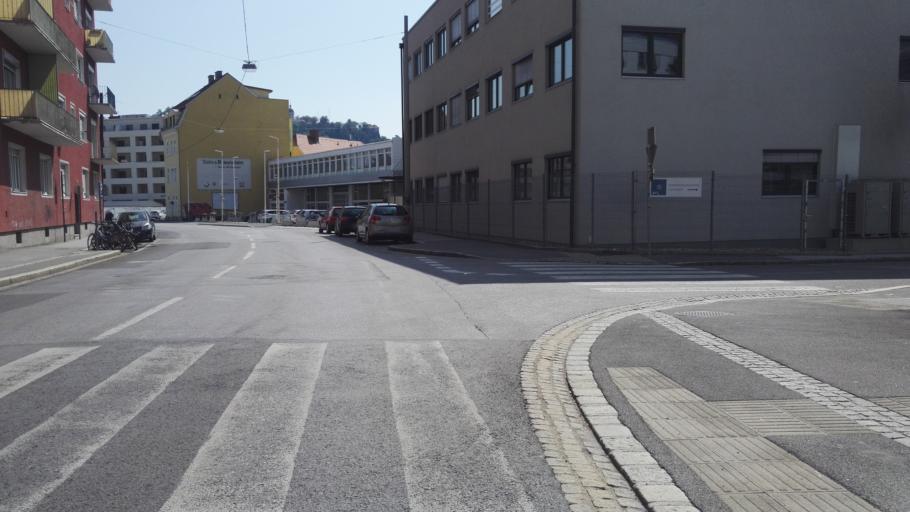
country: AT
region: Styria
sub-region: Graz Stadt
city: Graz
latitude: 47.0799
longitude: 15.4246
